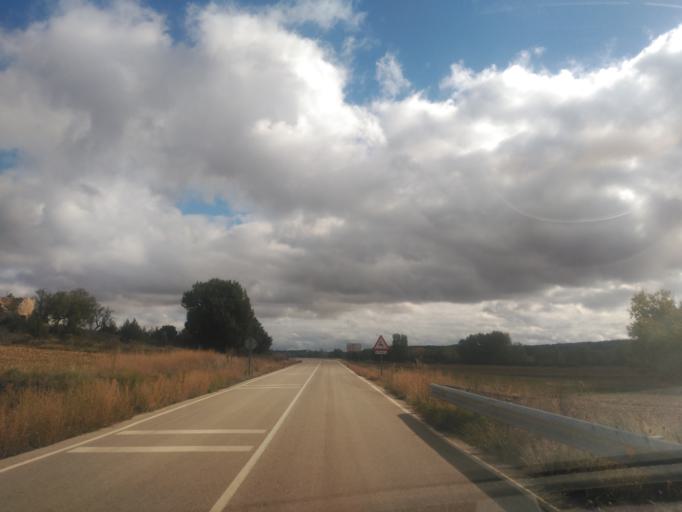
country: ES
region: Castille and Leon
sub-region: Provincia de Burgos
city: Brazacorta
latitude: 41.7199
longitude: -3.3403
